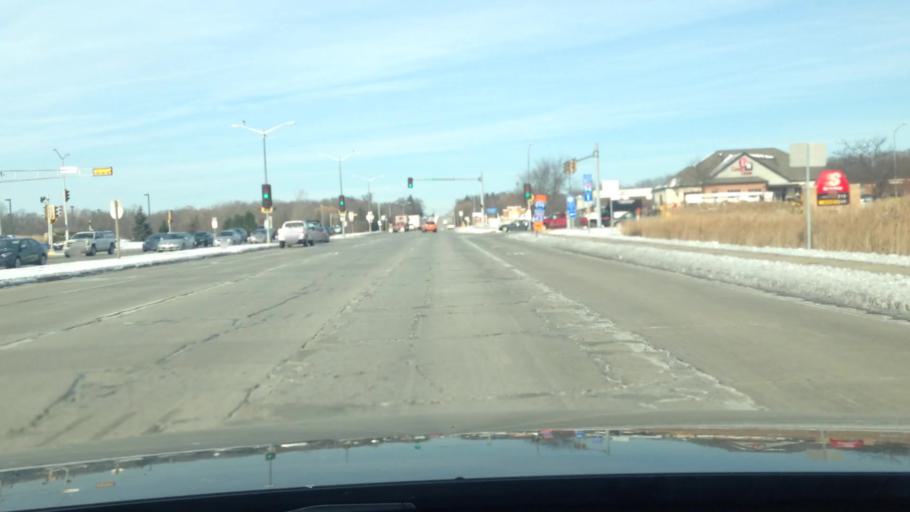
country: US
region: Wisconsin
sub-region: Waukesha County
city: New Berlin
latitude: 42.9553
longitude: -88.1088
